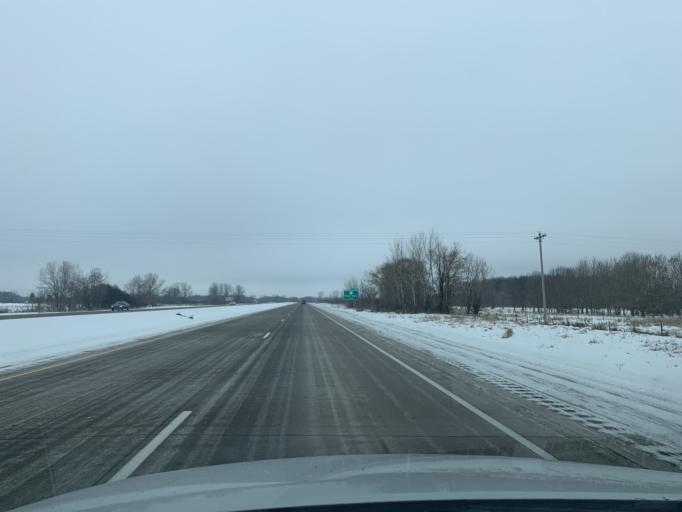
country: US
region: Minnesota
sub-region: Chisago County
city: Rush City
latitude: 45.7028
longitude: -92.9925
